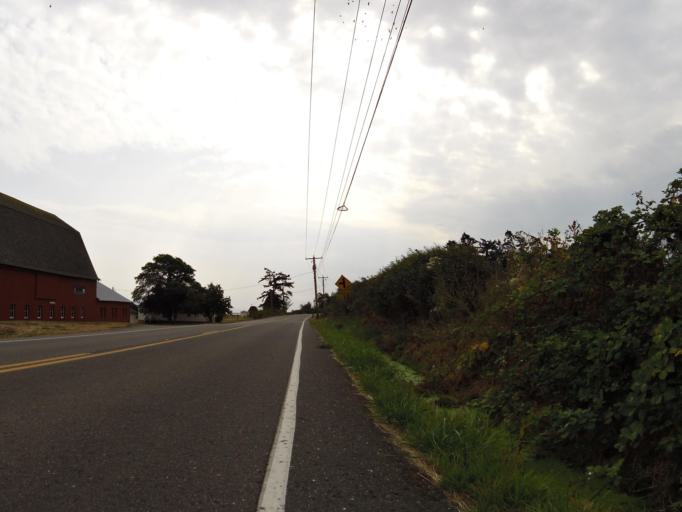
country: US
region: Washington
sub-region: Island County
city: Coupeville
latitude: 48.1898
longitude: -122.6680
